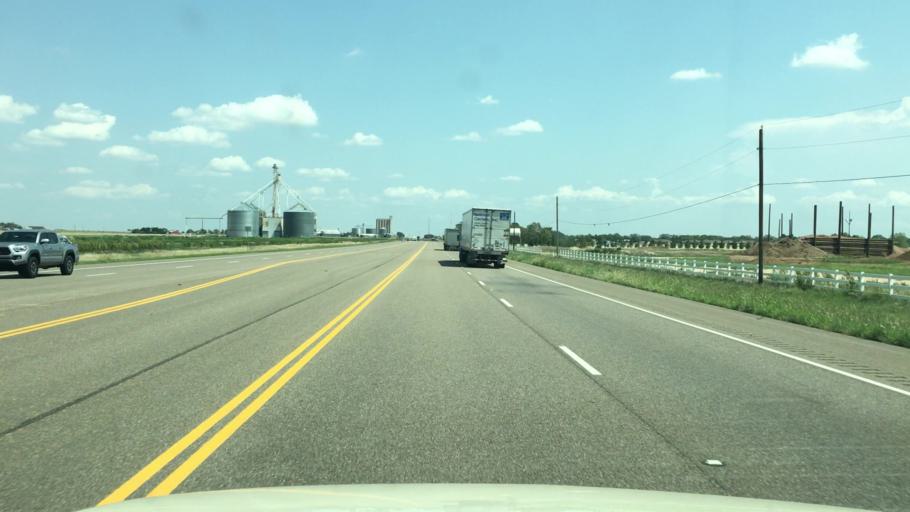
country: US
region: Texas
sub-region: Armstrong County
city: Claude
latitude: 35.1188
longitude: -101.3795
